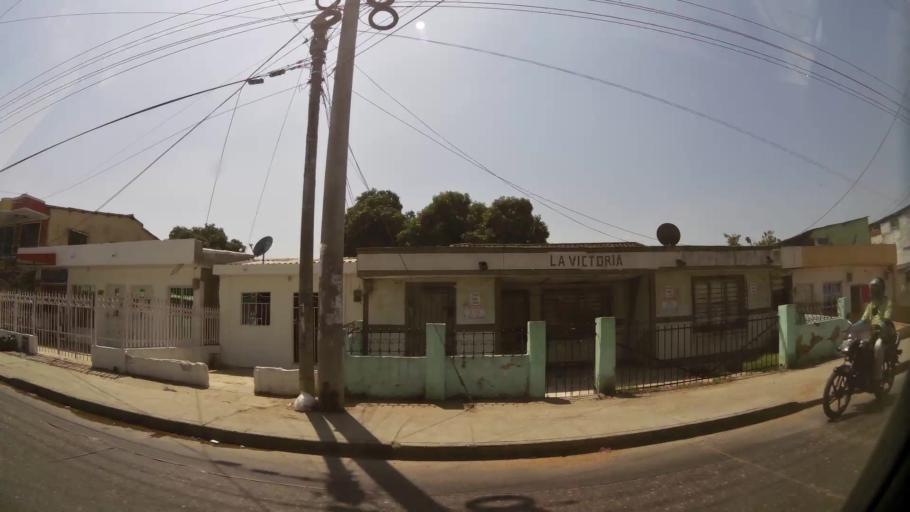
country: CO
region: Bolivar
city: Cartagena
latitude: 10.4058
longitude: -75.4877
